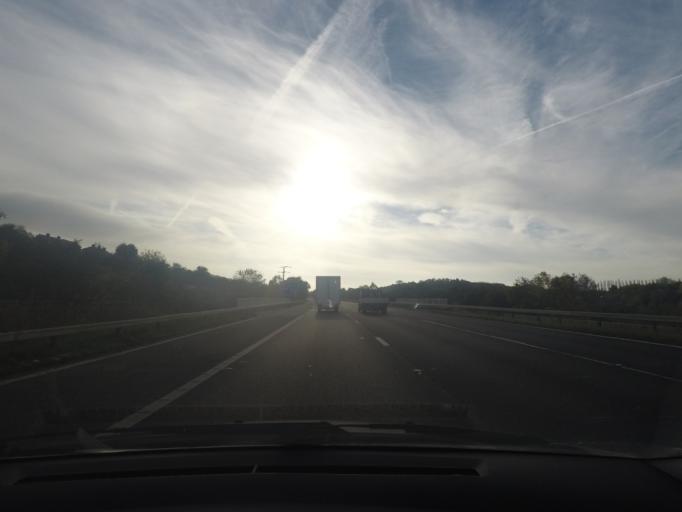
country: GB
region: England
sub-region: Barnsley
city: Dodworth
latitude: 53.5595
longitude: -1.5338
